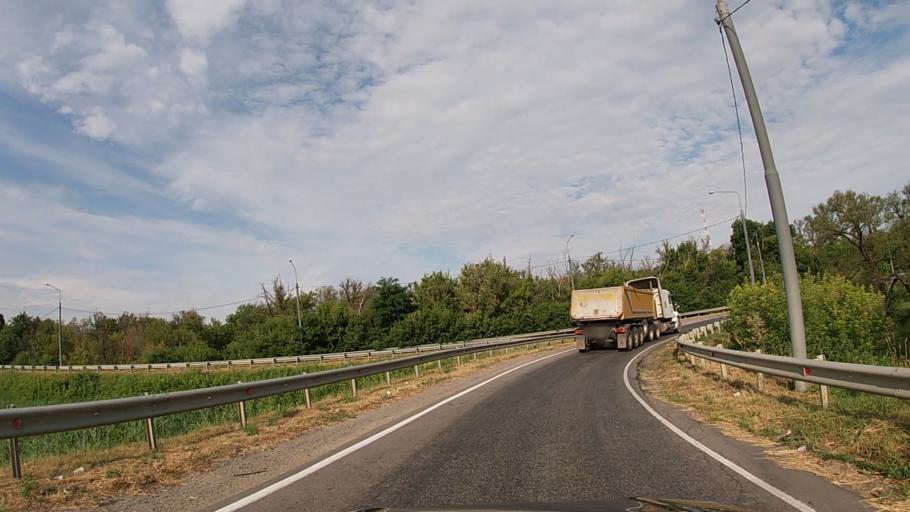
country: RU
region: Belgorod
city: Severnyy
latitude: 50.6339
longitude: 36.4653
